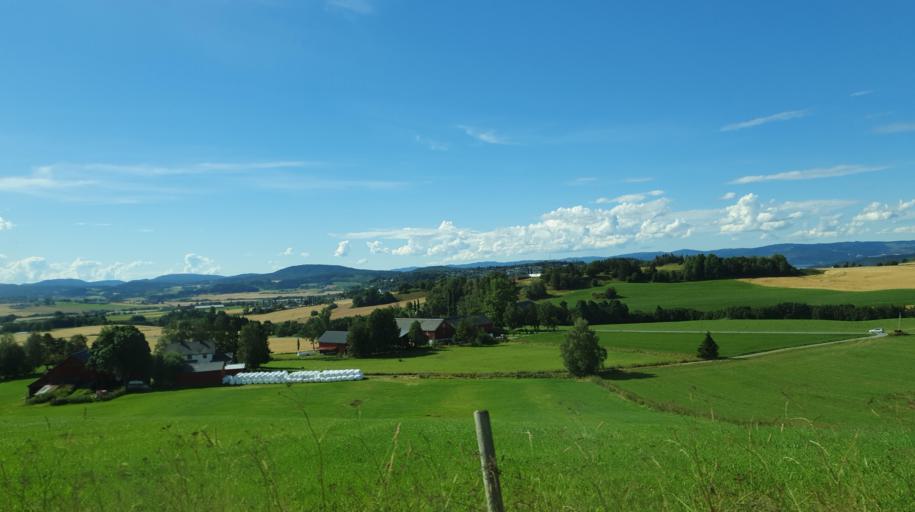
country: NO
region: Nord-Trondelag
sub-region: Levanger
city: Skogn
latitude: 63.6974
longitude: 11.2359
